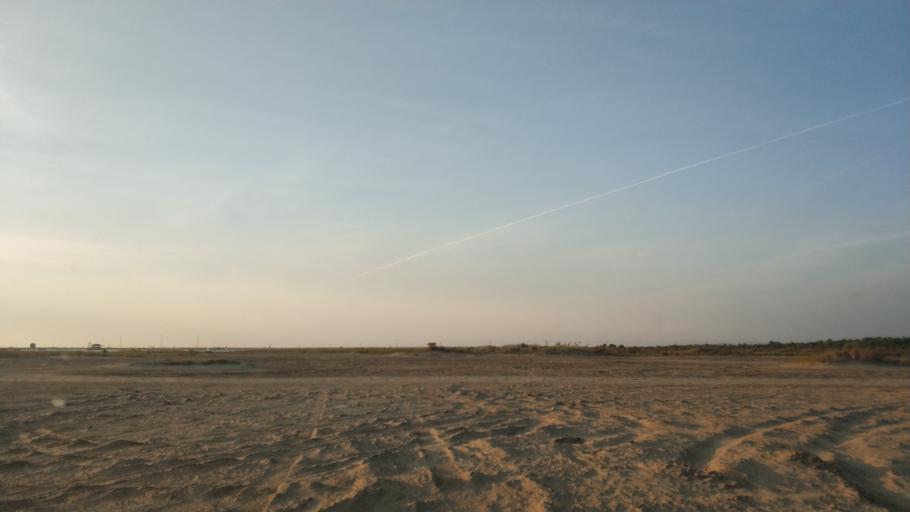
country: AL
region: Fier
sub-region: Rrethi i Lushnjes
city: Divjake
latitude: 40.9707
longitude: 19.4763
